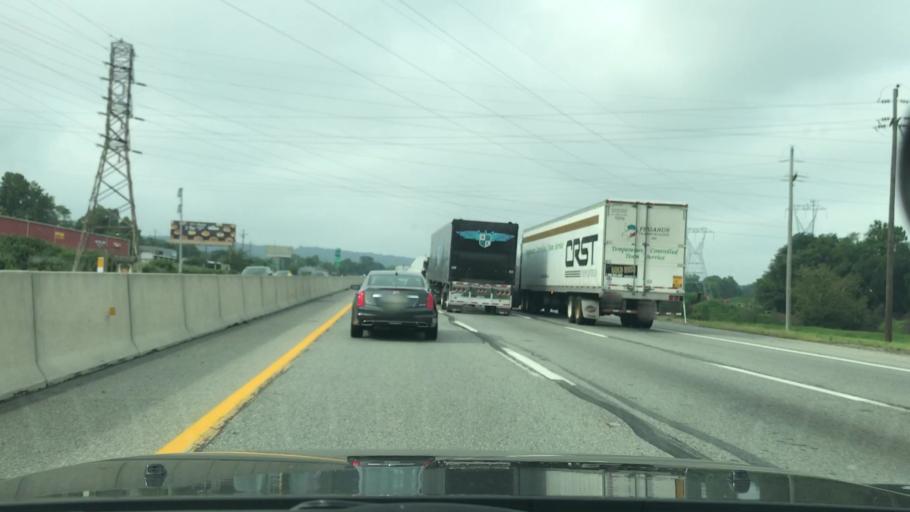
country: US
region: Pennsylvania
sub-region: Montgomery County
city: Bridgeport
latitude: 40.0950
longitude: -75.3444
